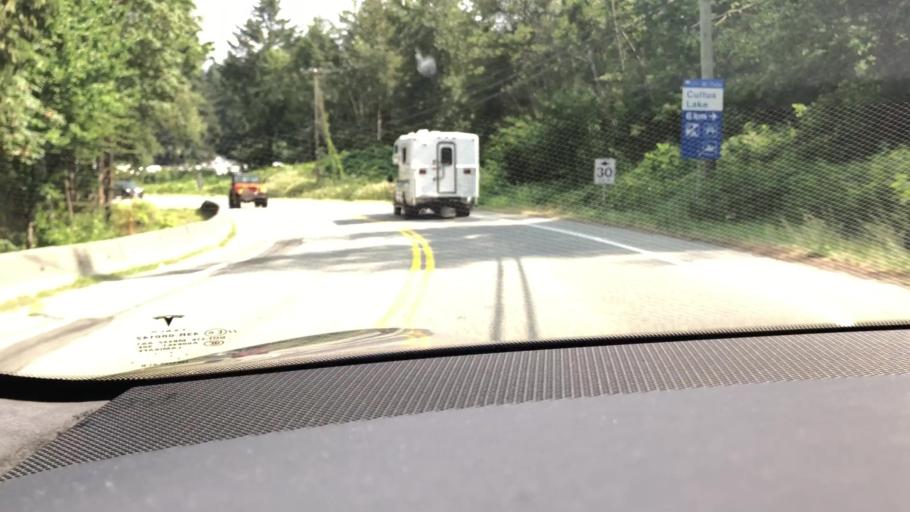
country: CA
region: British Columbia
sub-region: Fraser Valley Regional District
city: Chilliwack
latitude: 49.0949
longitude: -121.9764
